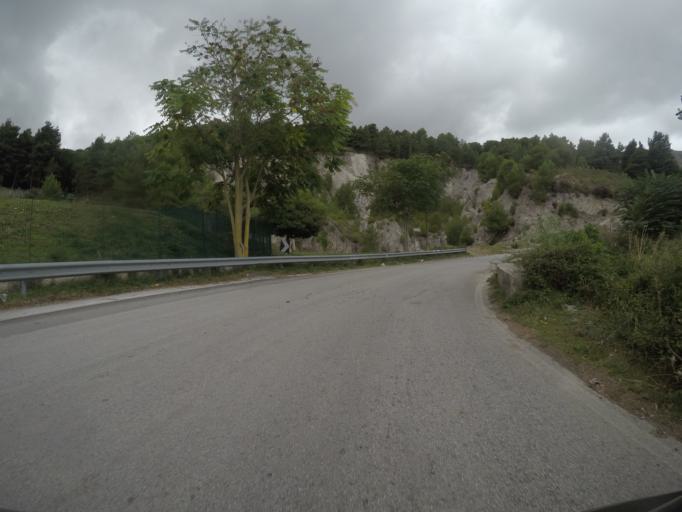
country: IT
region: Sicily
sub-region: Palermo
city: Montelepre
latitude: 38.1153
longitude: 13.1709
